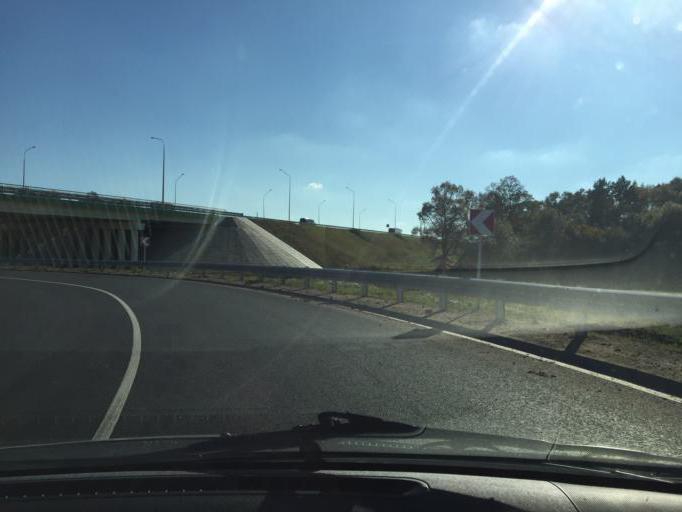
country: BY
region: Minsk
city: Slutsk
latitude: 52.9921
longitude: 27.5065
